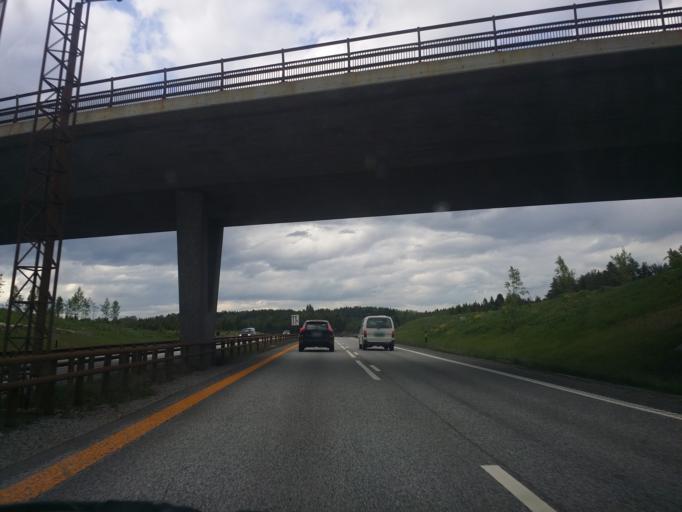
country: NO
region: Akershus
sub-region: Eidsvoll
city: Raholt
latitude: 60.3314
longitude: 11.1901
